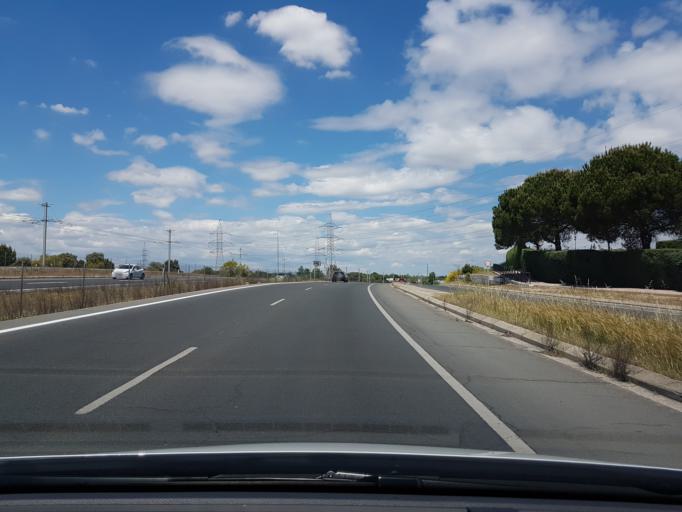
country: ES
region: Madrid
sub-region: Provincia de Madrid
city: Pozuelo de Alarcon
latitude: 40.4250
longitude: -3.8068
